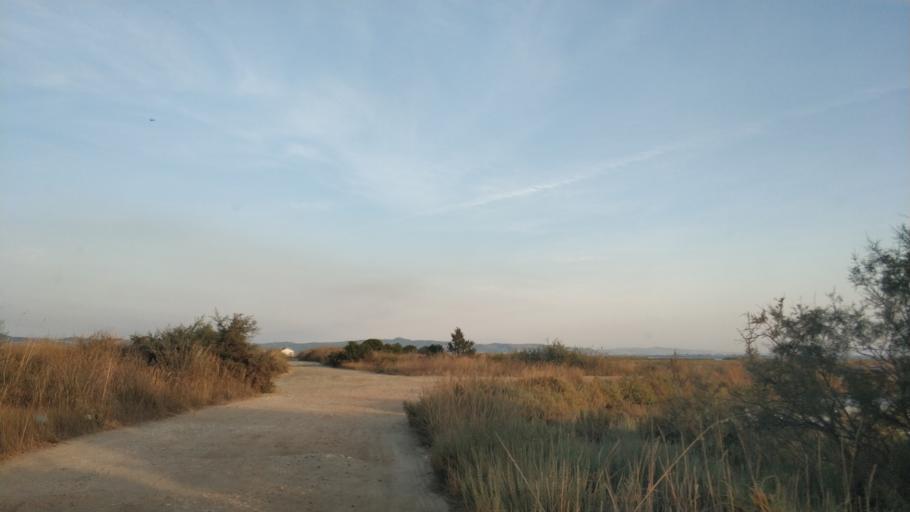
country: AL
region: Fier
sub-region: Rrethi i Lushnjes
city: Divjake
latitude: 40.9511
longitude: 19.4771
